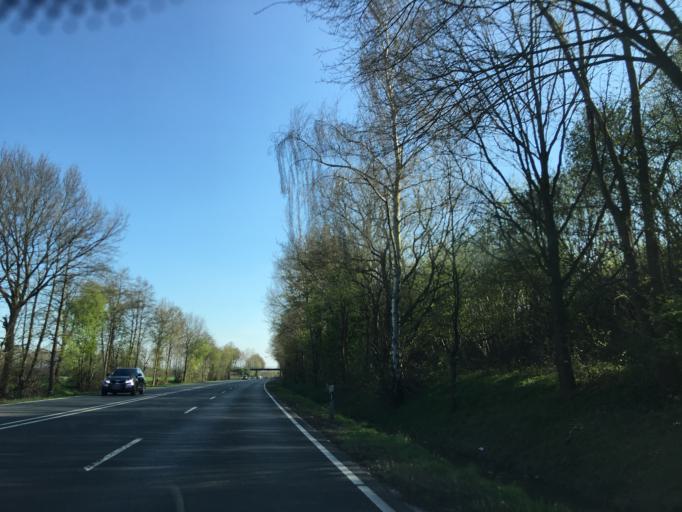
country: DE
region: North Rhine-Westphalia
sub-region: Regierungsbezirk Munster
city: Greven
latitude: 52.1017
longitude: 7.6293
